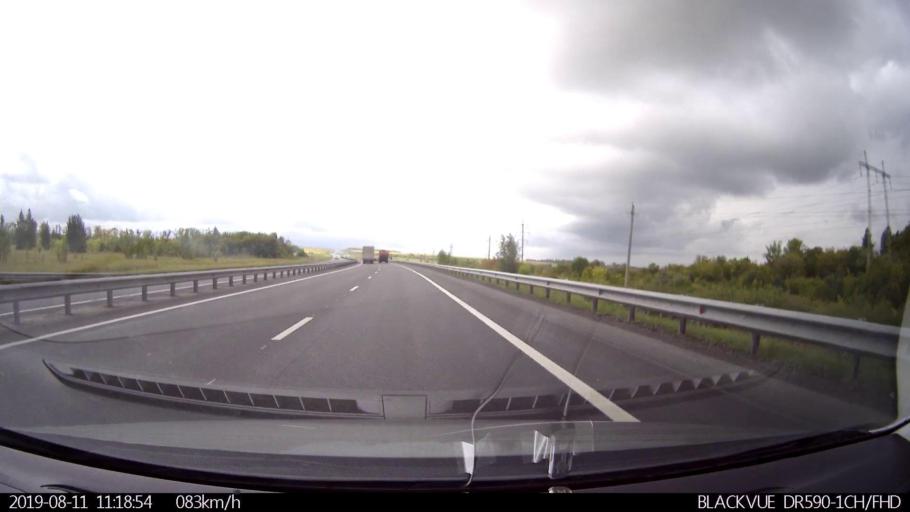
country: RU
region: Ulyanovsk
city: Novoul'yanovsk
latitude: 54.1752
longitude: 48.2652
